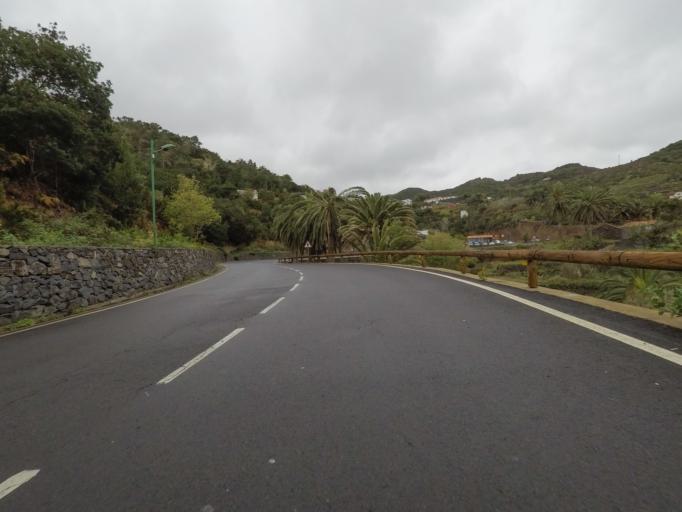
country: ES
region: Canary Islands
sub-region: Provincia de Santa Cruz de Tenerife
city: Agulo
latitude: 28.1841
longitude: -17.2223
